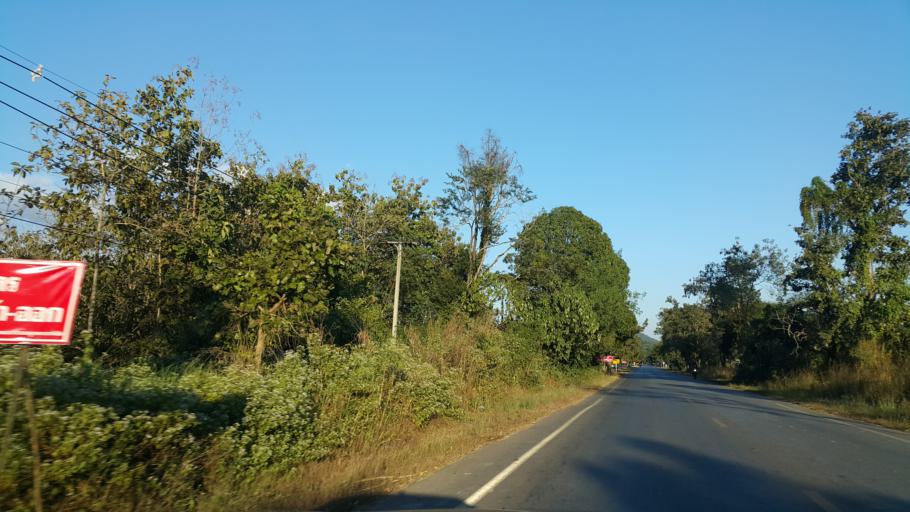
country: TH
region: Sukhothai
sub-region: Amphoe Si Satchanalai
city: Si Satchanalai
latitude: 17.5509
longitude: 99.8636
